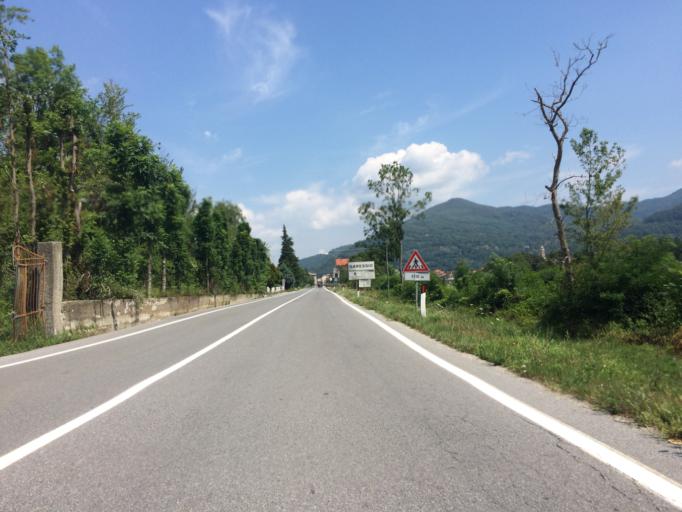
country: IT
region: Piedmont
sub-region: Provincia di Cuneo
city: Garessio
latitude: 44.1977
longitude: 8.0118
